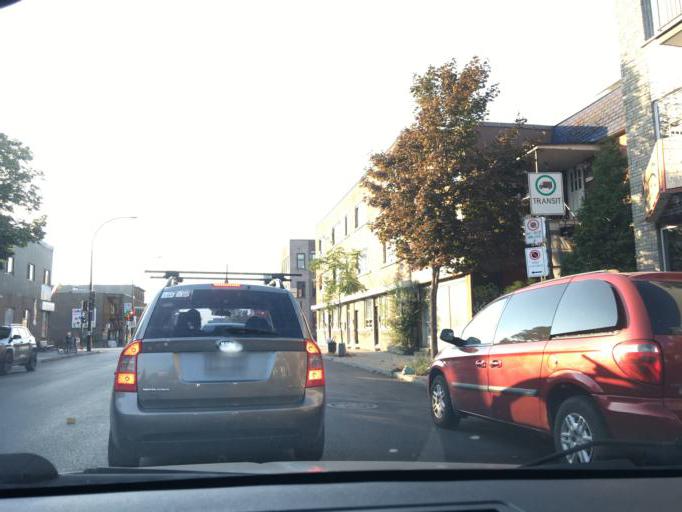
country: CA
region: Quebec
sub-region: Montreal
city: Montreal
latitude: 45.5413
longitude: -73.5926
